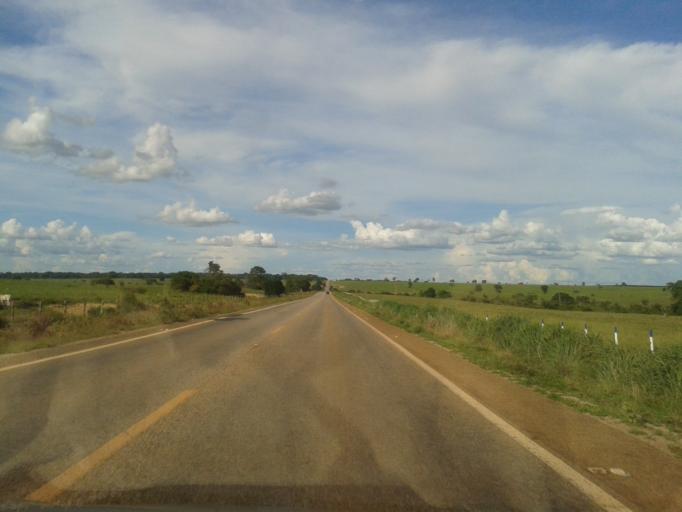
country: BR
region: Goias
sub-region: Mozarlandia
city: Mozarlandia
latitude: -14.3546
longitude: -50.4239
